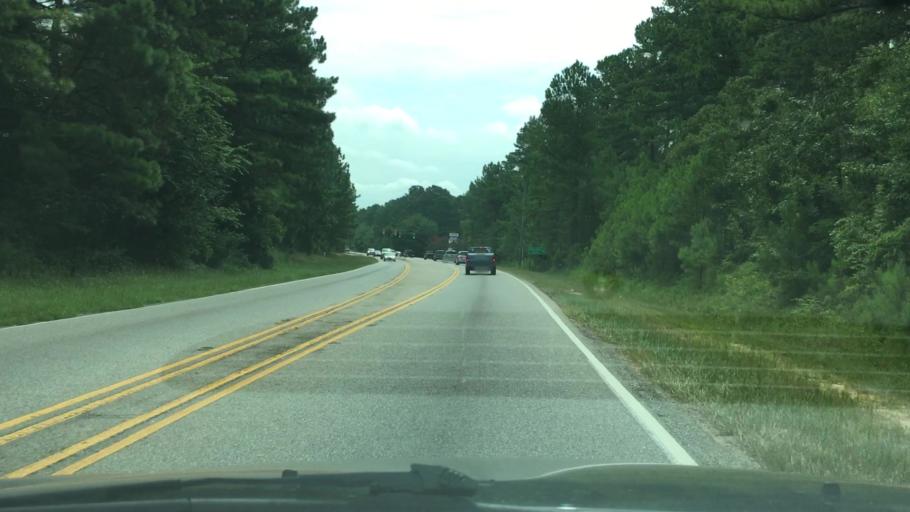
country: US
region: South Carolina
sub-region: Aiken County
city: Warrenville
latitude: 33.5296
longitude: -81.7645
